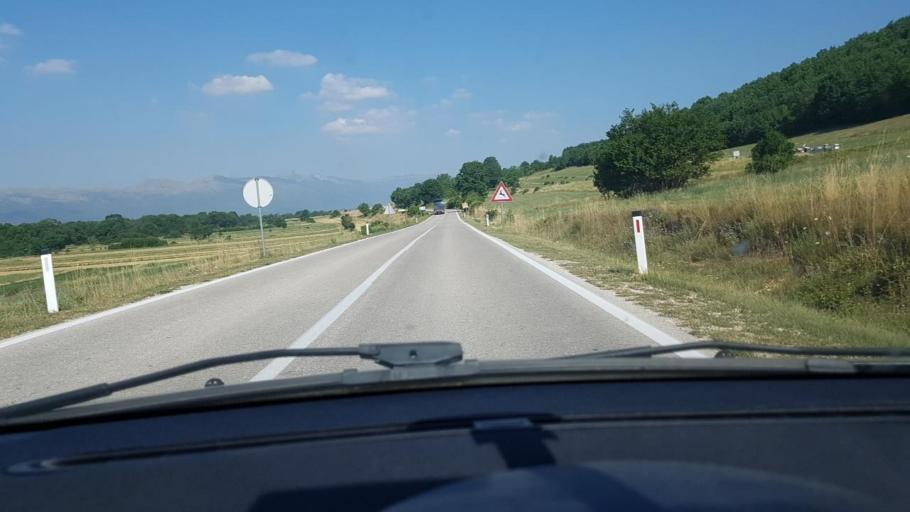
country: BA
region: Federation of Bosnia and Herzegovina
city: Orguz
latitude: 43.8873
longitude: 16.8349
